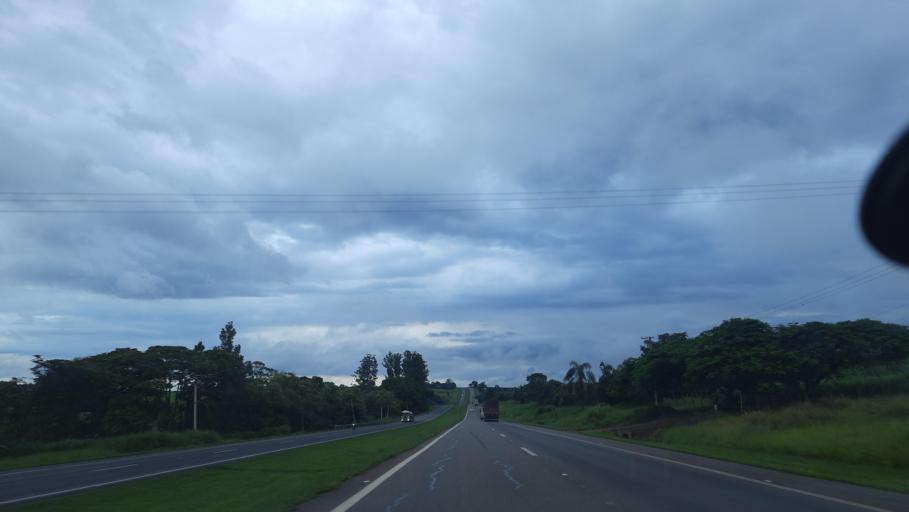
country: BR
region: Sao Paulo
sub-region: Moji-Guacu
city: Mogi-Gaucu
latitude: -22.2377
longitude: -46.9784
